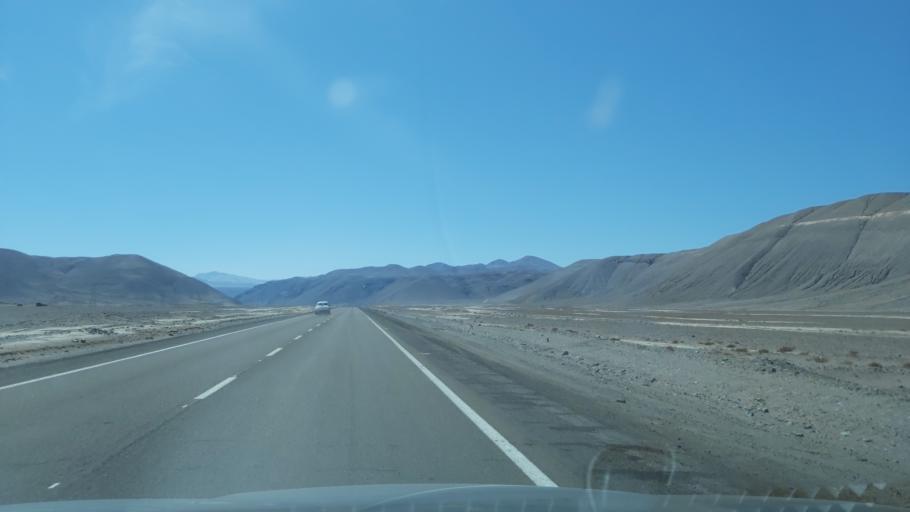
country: CL
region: Atacama
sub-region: Provincia de Chanaral
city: Diego de Almagro
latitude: -26.3512
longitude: -69.8864
